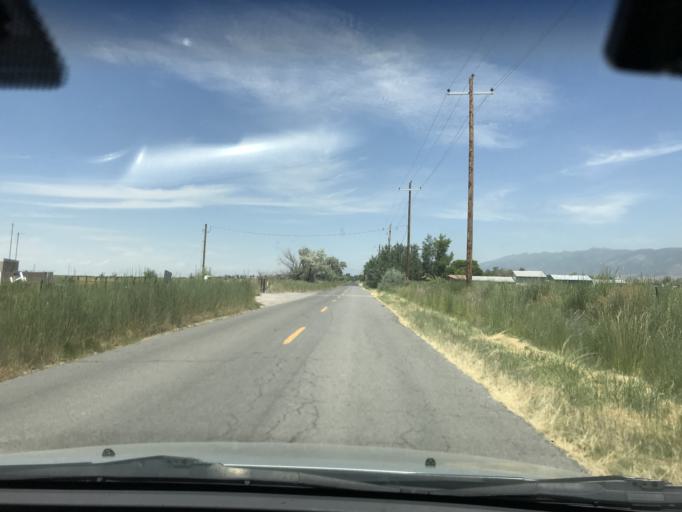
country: US
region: Utah
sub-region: Davis County
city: North Salt Lake
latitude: 40.8234
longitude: -111.9535
